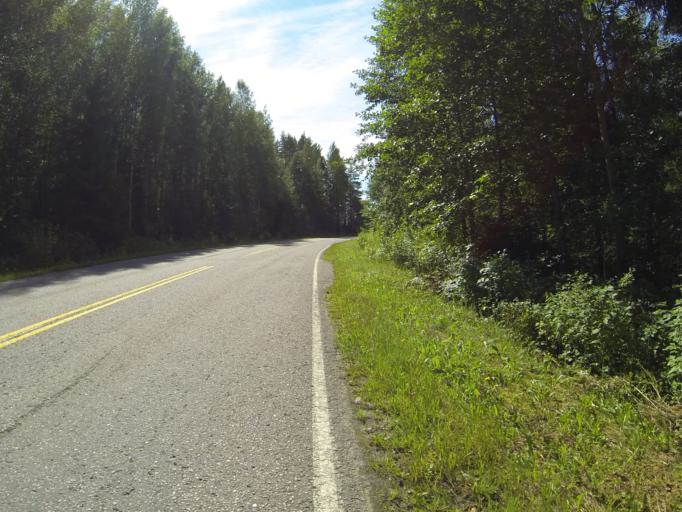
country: FI
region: Varsinais-Suomi
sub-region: Salo
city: Saerkisalo
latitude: 60.2716
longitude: 22.9832
